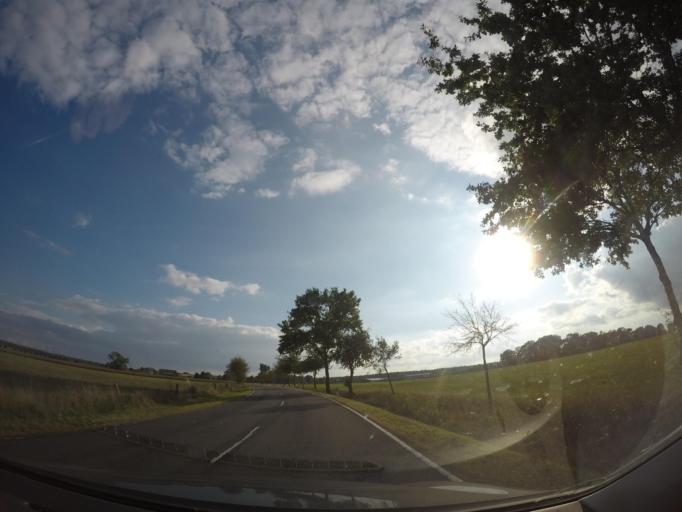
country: DE
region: Saxony-Anhalt
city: Weferlingen
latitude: 52.3750
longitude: 11.0991
